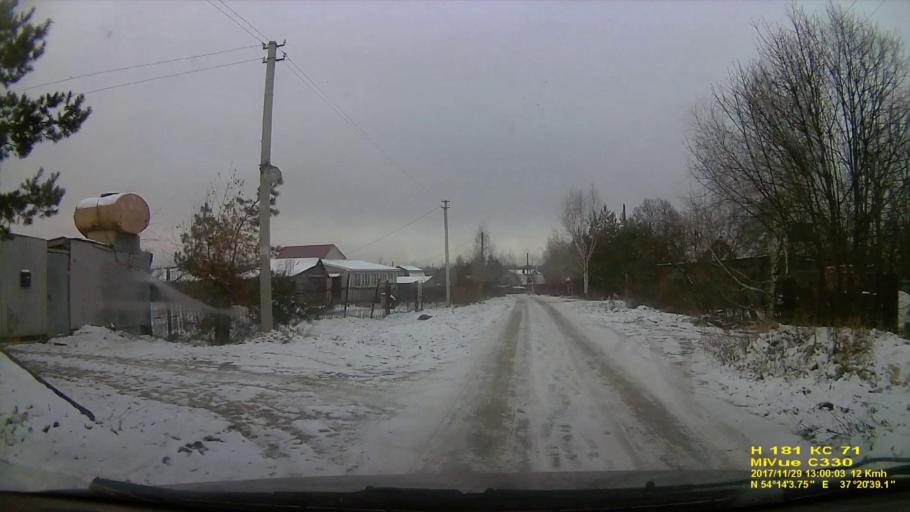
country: RU
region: Tula
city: Leninskiy
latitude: 54.2344
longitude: 37.3440
